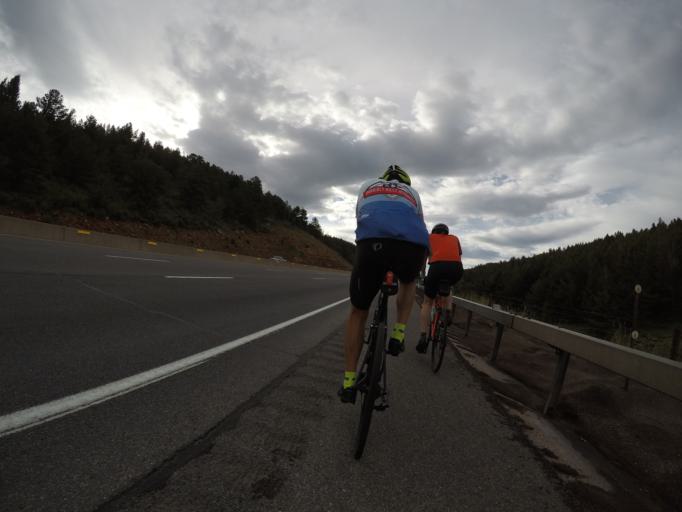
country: US
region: Wyoming
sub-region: Albany County
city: Laramie
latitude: 41.2608
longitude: -105.4579
